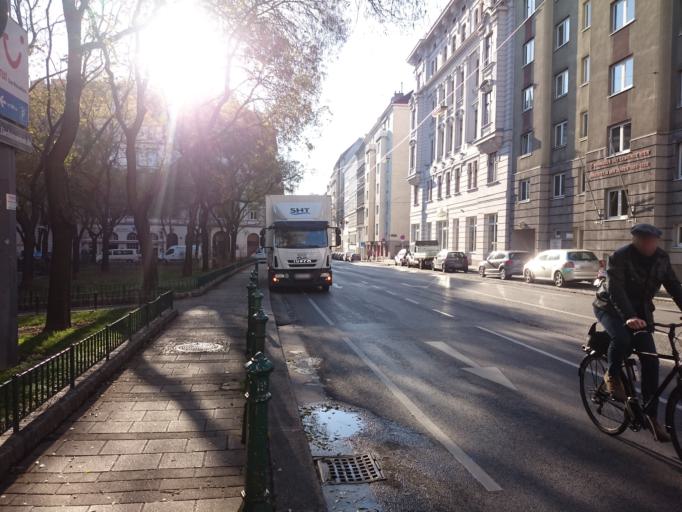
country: AT
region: Vienna
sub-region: Wien Stadt
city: Vienna
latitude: 48.2305
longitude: 16.3561
